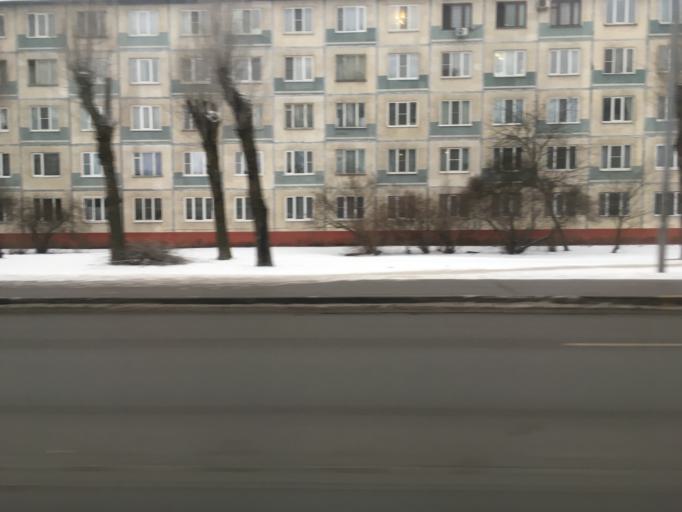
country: RU
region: St.-Petersburg
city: Obukhovo
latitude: 59.8676
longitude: 30.4425
